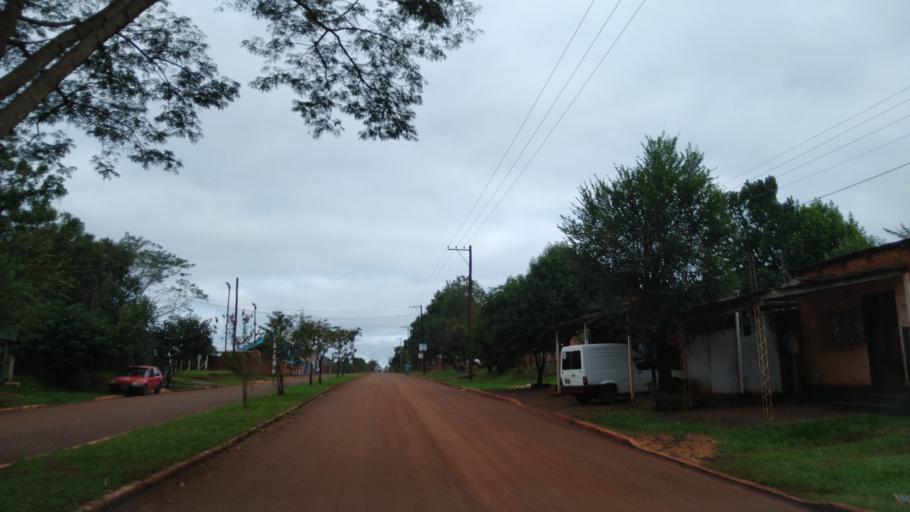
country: AR
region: Misiones
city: Jardin America
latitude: -27.0302
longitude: -55.2350
